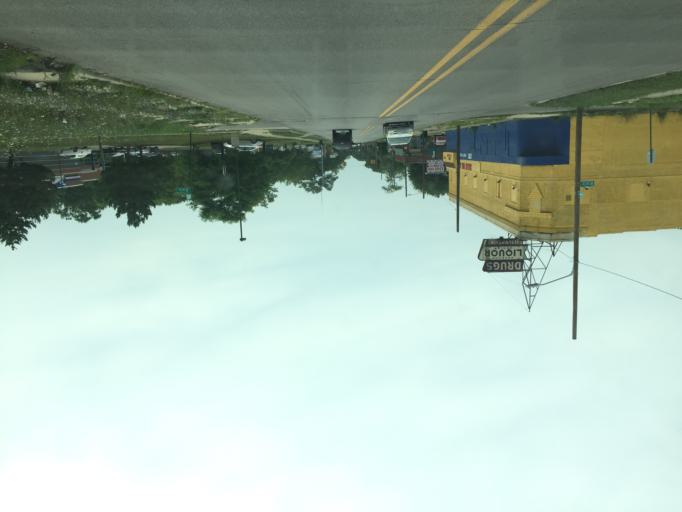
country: US
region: Michigan
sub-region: Wayne County
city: Redford
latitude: 42.4006
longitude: -83.2454
